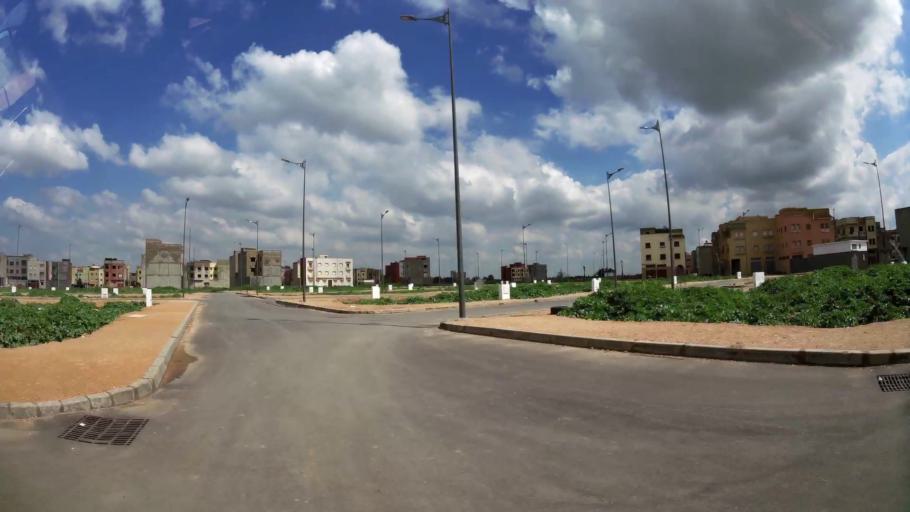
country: MA
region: Grand Casablanca
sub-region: Mediouna
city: Mediouna
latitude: 33.3664
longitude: -7.5324
